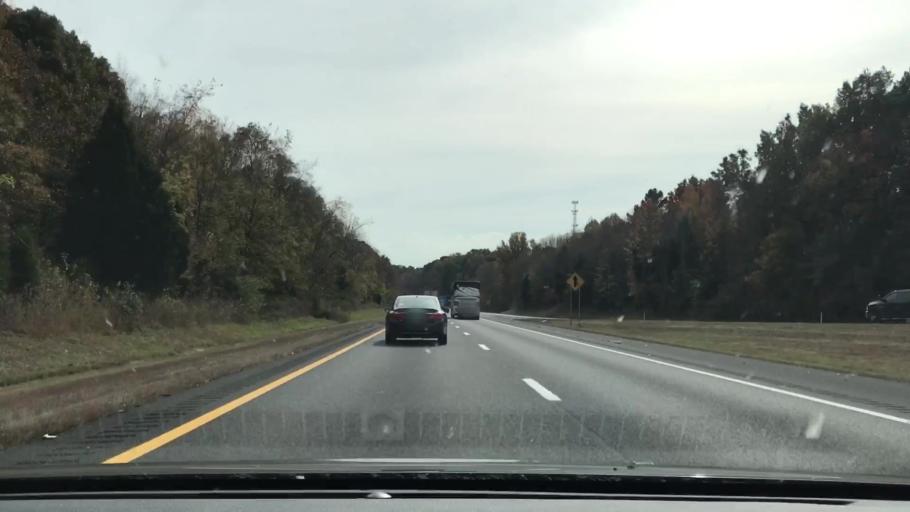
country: US
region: Tennessee
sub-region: Montgomery County
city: Clarksville
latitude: 36.5536
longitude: -87.2490
